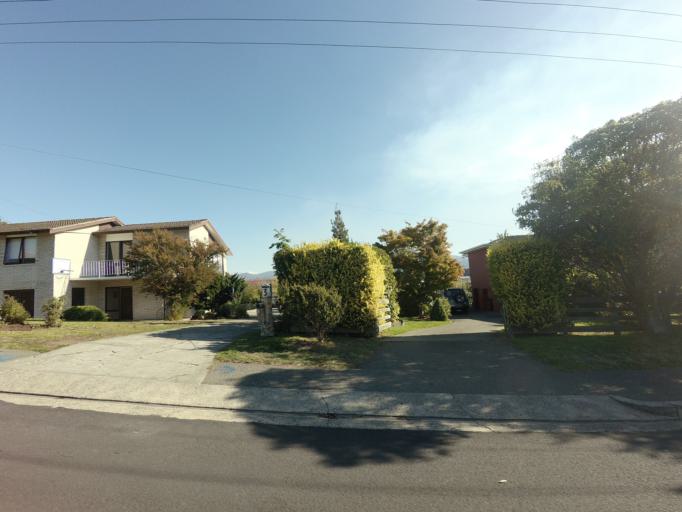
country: AU
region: Tasmania
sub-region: Clarence
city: Bellerive
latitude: -42.8720
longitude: 147.3532
